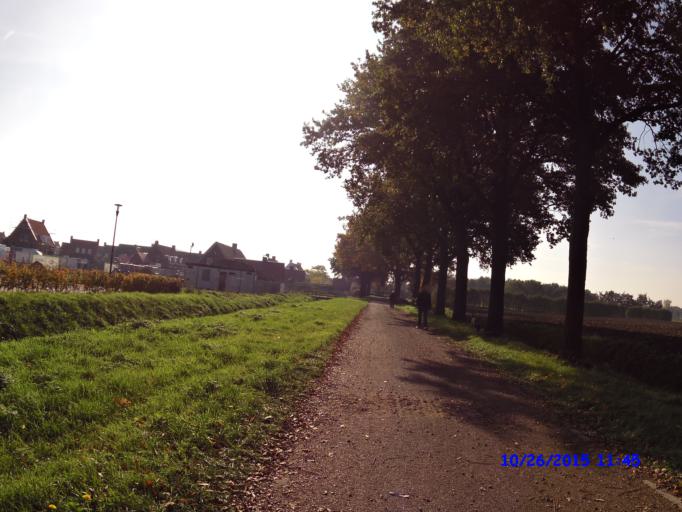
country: NL
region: North Brabant
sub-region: Gemeente Geldrop-Mierlo
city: Mierlo
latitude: 51.4556
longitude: 5.6058
